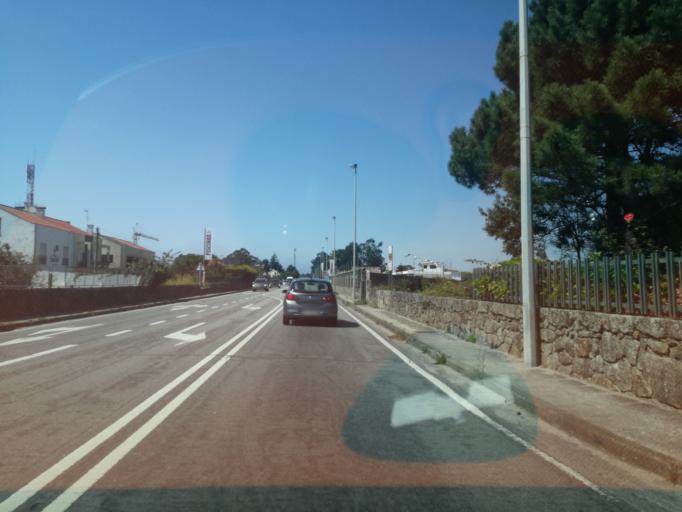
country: PT
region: Braga
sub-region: Esposende
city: Esposende
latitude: 41.5331
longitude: -8.7769
